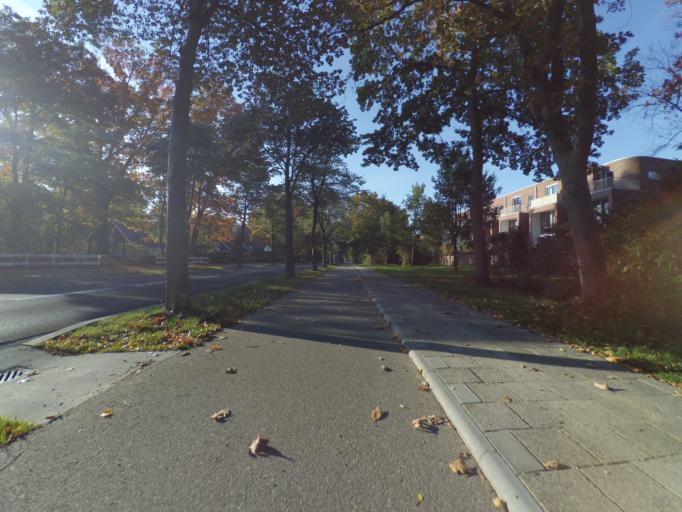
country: NL
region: Utrecht
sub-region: Gemeente Zeist
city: Zeist
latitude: 52.0926
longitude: 5.2514
